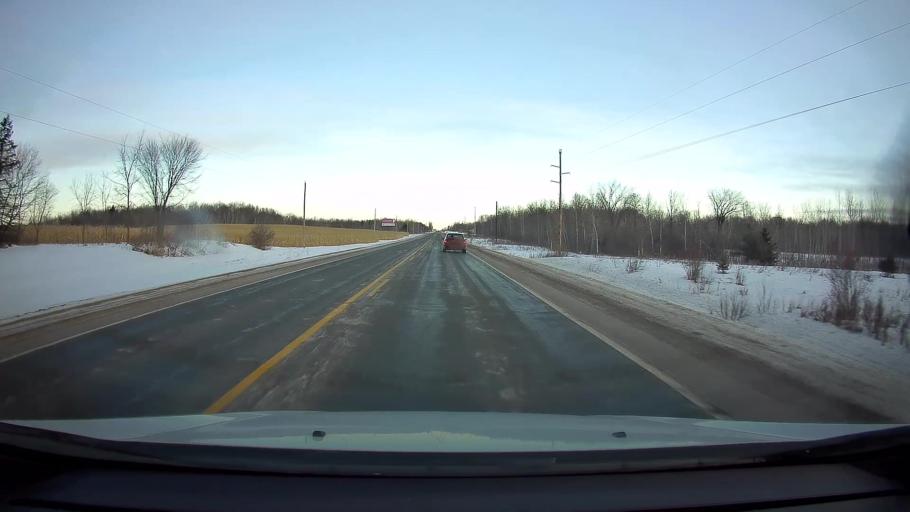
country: US
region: Wisconsin
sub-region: Barron County
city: Turtle Lake
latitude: 45.3533
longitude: -92.1669
